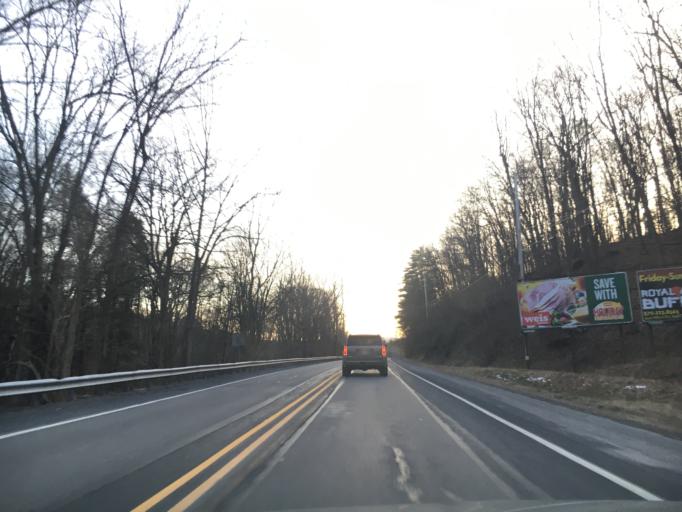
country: US
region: Pennsylvania
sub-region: Monroe County
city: East Stroudsburg
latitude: 41.0124
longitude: -75.1314
